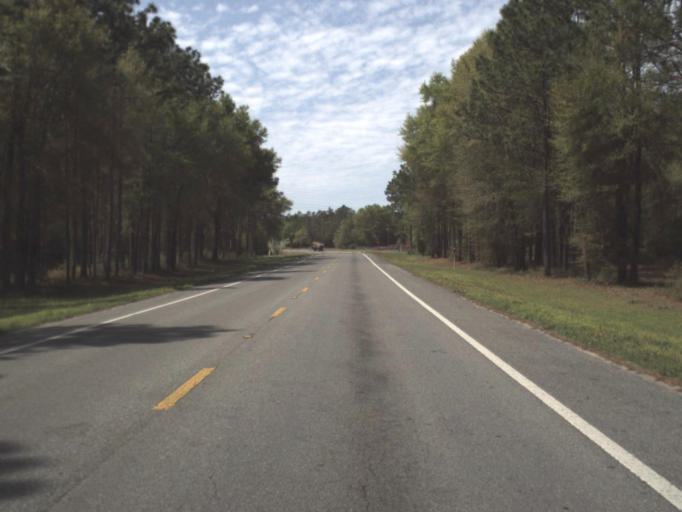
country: US
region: Florida
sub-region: Okaloosa County
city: Crestview
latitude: 30.7412
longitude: -86.6496
